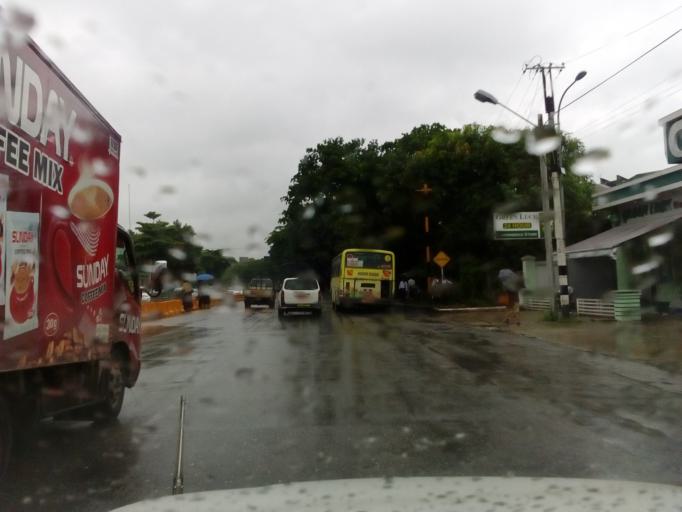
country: MM
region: Yangon
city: Yangon
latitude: 16.8151
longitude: 96.1726
